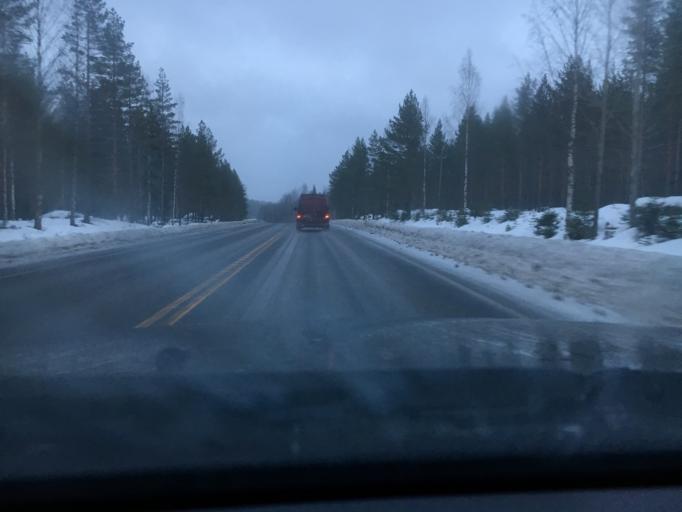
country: FI
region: Central Finland
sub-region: Jyvaeskylae
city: Hankasalmi
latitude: 62.4044
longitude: 26.6610
